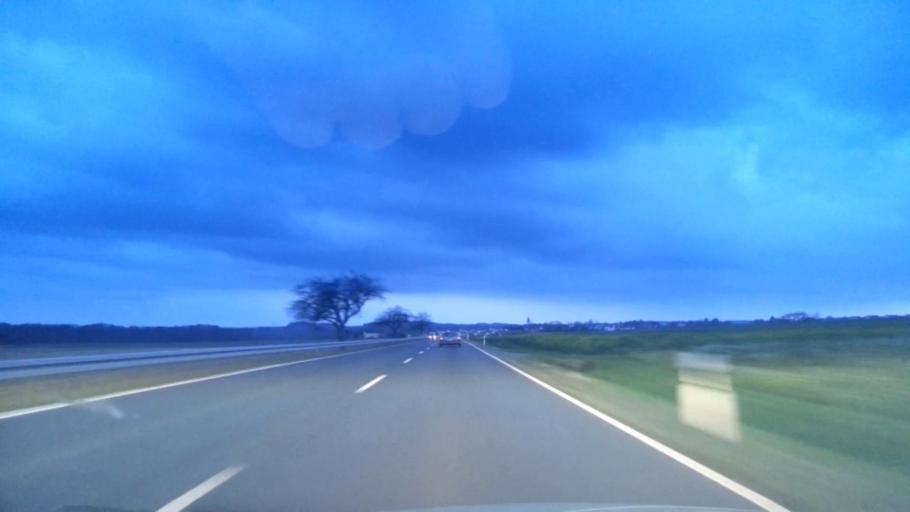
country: DE
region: Bavaria
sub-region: Upper Palatinate
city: Kulmain
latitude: 49.8972
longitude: 11.9173
